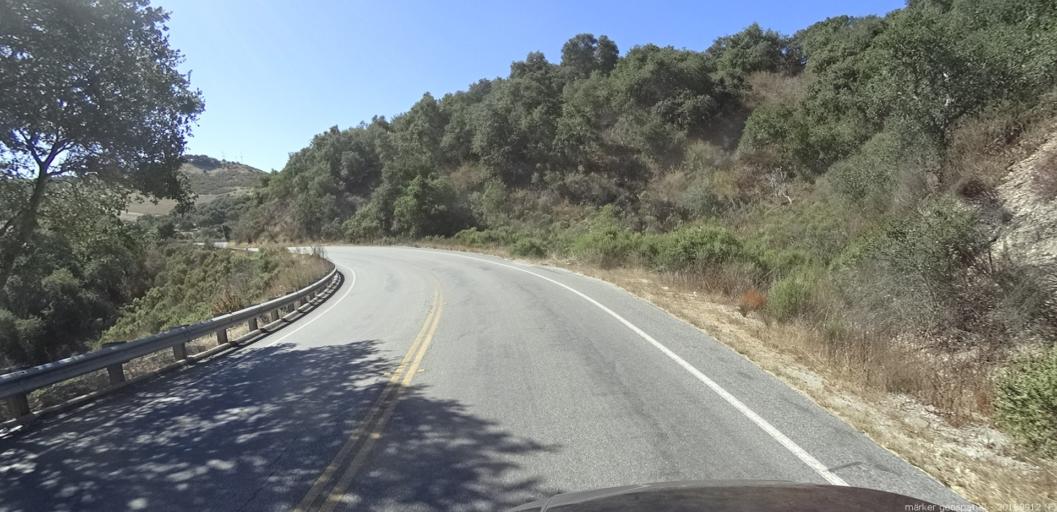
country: US
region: California
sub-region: Monterey County
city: Carmel Valley Village
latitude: 36.5328
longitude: -121.7498
